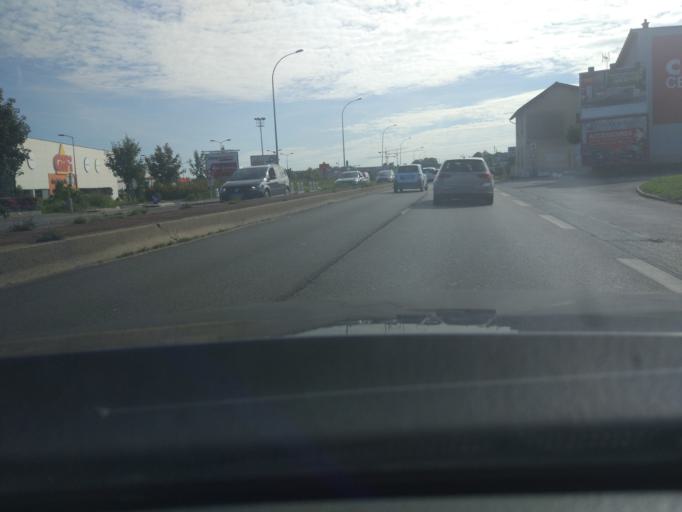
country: FR
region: Ile-de-France
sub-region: Departement de l'Essonne
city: La Ville-du-Bois
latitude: 48.6552
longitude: 2.2740
